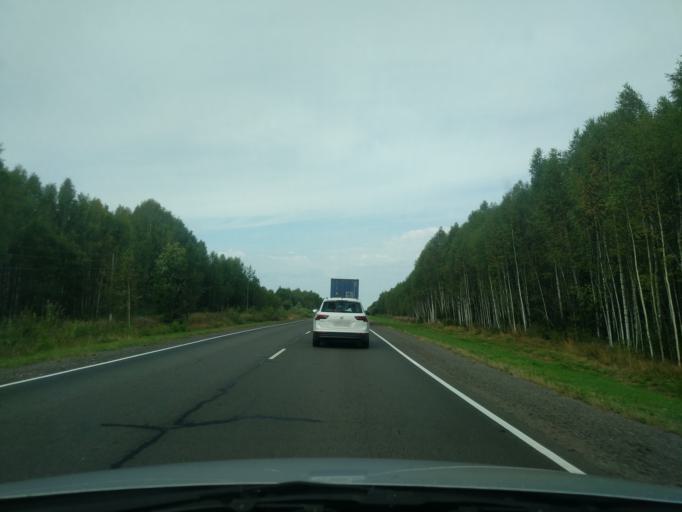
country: RU
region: Kirov
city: Leninskoye
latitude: 58.2848
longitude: 47.2534
